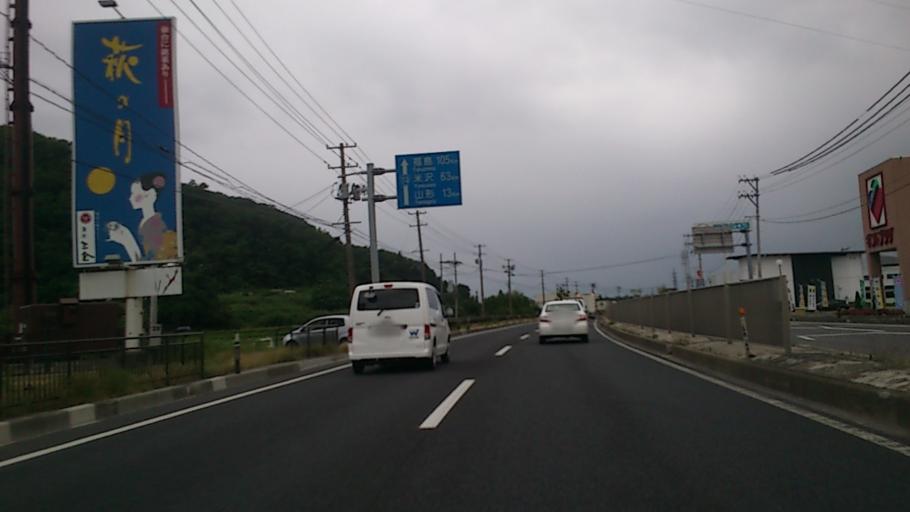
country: JP
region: Yamagata
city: Tendo
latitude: 38.3522
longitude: 140.3869
